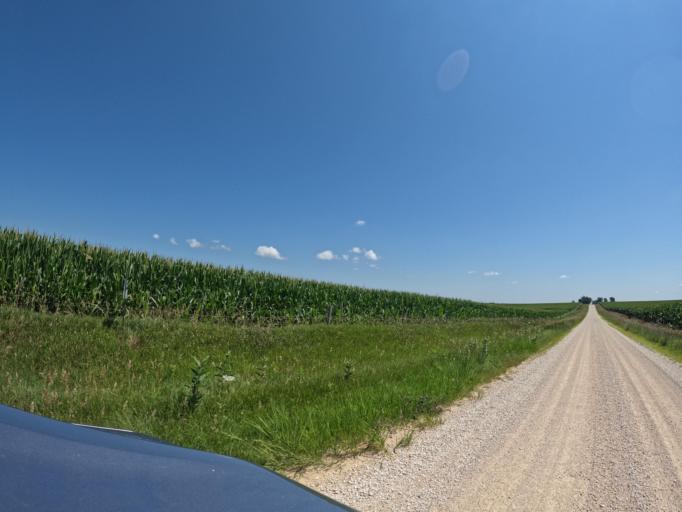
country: US
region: Iowa
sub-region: Clinton County
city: De Witt
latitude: 41.7720
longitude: -90.4101
